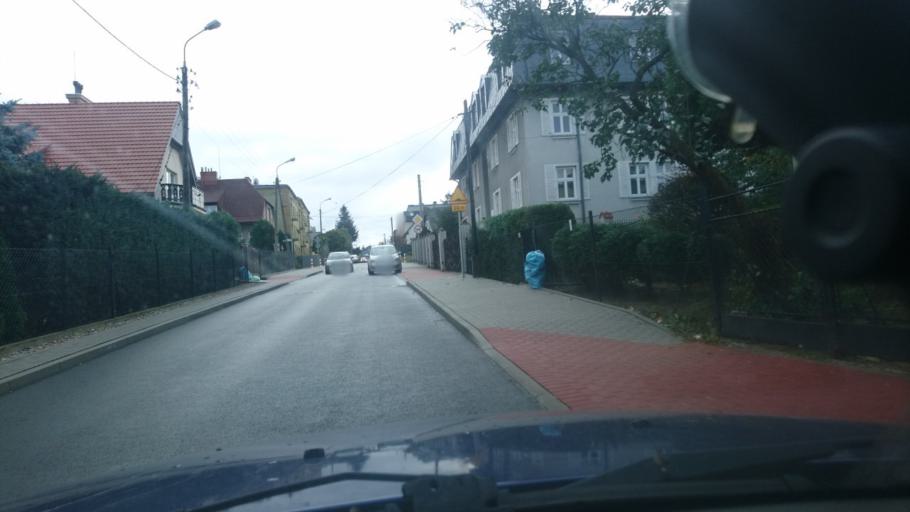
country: PL
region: Silesian Voivodeship
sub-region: Bielsko-Biala
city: Bielsko-Biala
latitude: 49.8272
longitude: 19.0268
